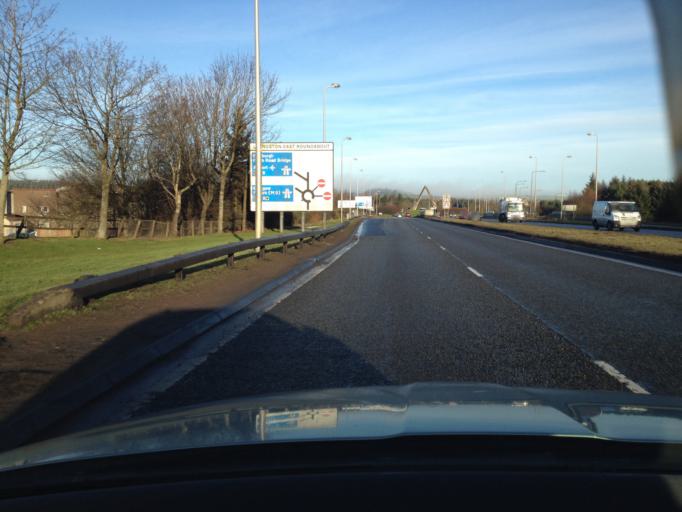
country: GB
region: Scotland
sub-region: West Lothian
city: Livingston
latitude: 55.9125
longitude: -3.5220
